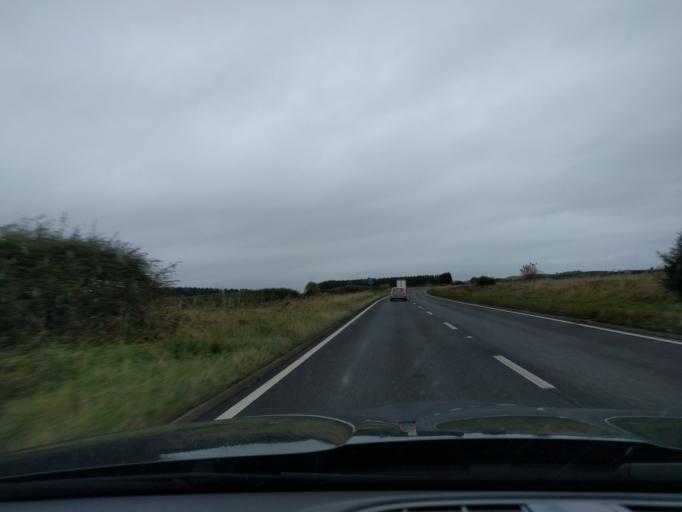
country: GB
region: England
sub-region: Northumberland
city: Ancroft
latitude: 55.6961
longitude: -1.9600
